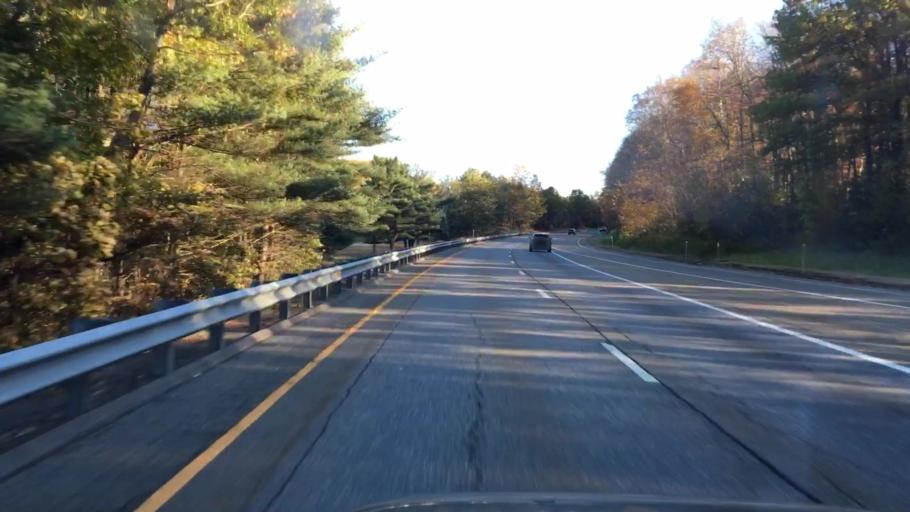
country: US
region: Connecticut
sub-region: Litchfield County
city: Northwest Harwinton
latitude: 41.7248
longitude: -73.0988
